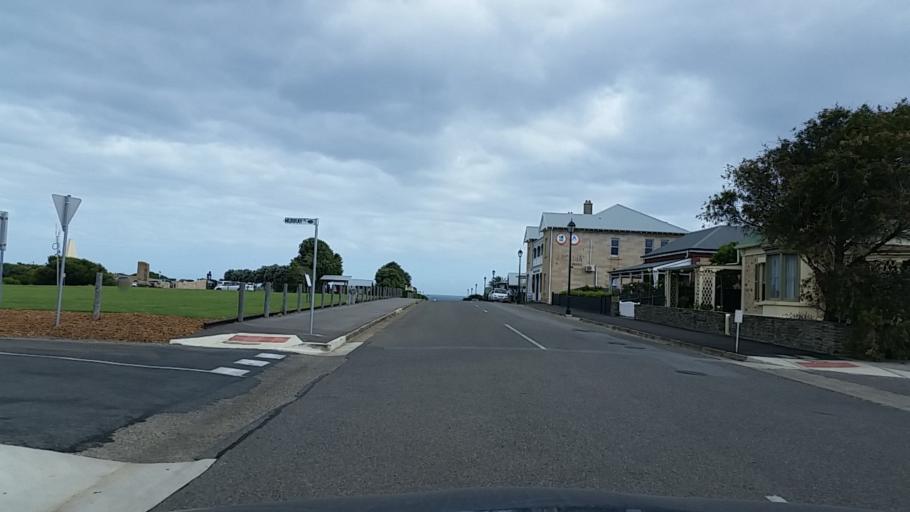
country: AU
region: South Australia
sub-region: Alexandrina
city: Port Elliot
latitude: -35.5344
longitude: 138.6820
